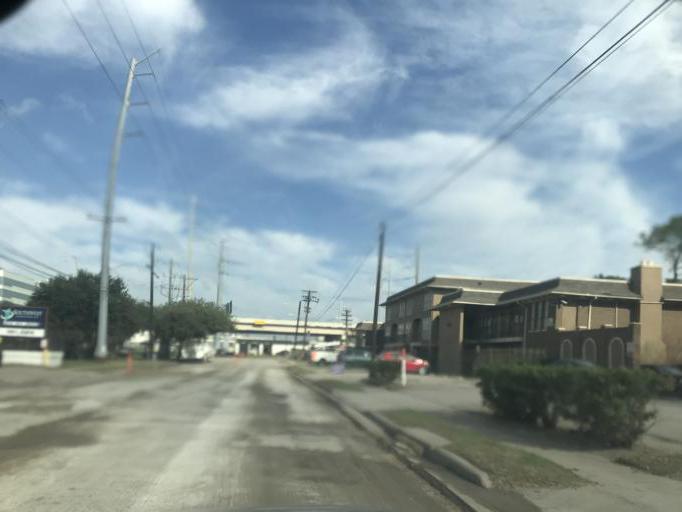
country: US
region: Texas
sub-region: Harris County
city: Bellaire
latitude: 29.7233
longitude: -95.4807
